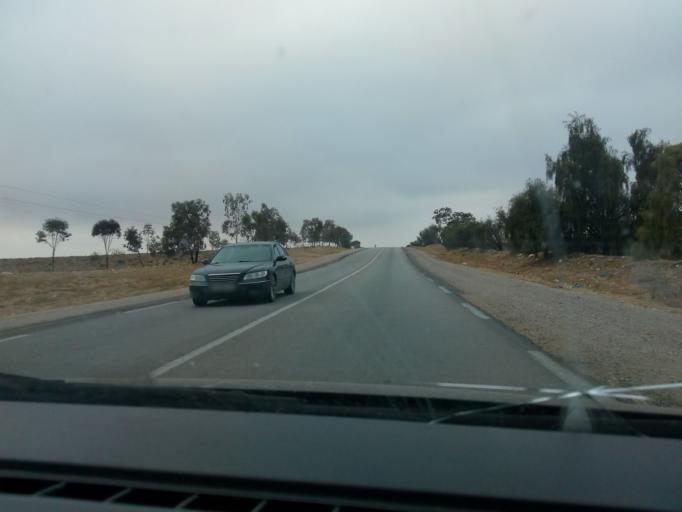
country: TN
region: Madanin
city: Medenine
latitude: 33.2680
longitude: 10.4667
